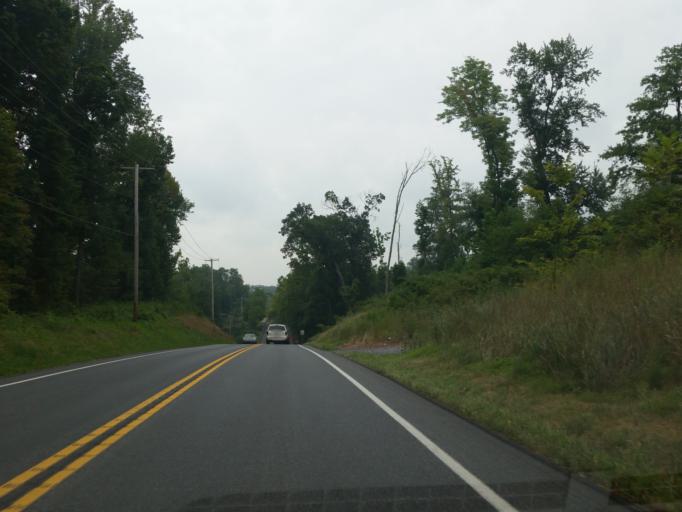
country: US
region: Pennsylvania
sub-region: Lancaster County
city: Brickerville
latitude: 40.2389
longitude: -76.2985
